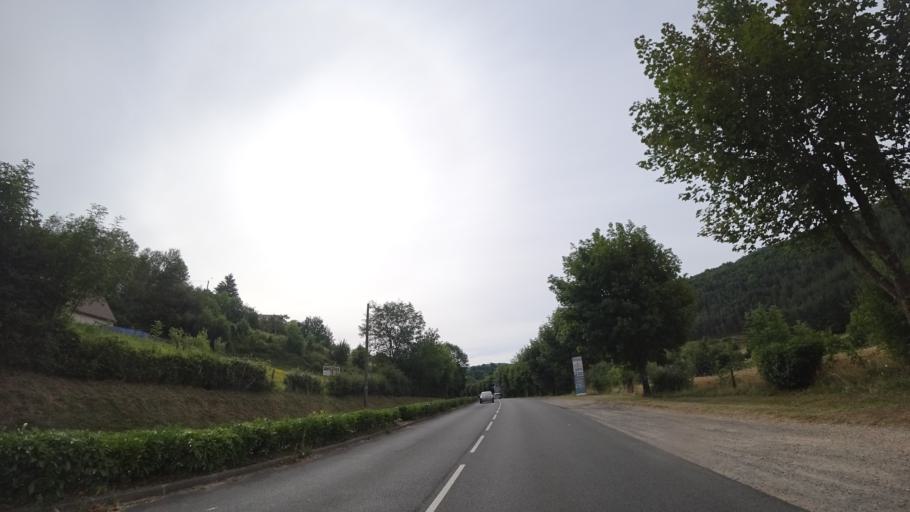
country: FR
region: Languedoc-Roussillon
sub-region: Departement de la Lozere
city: La Canourgue
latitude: 44.4348
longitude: 3.2044
